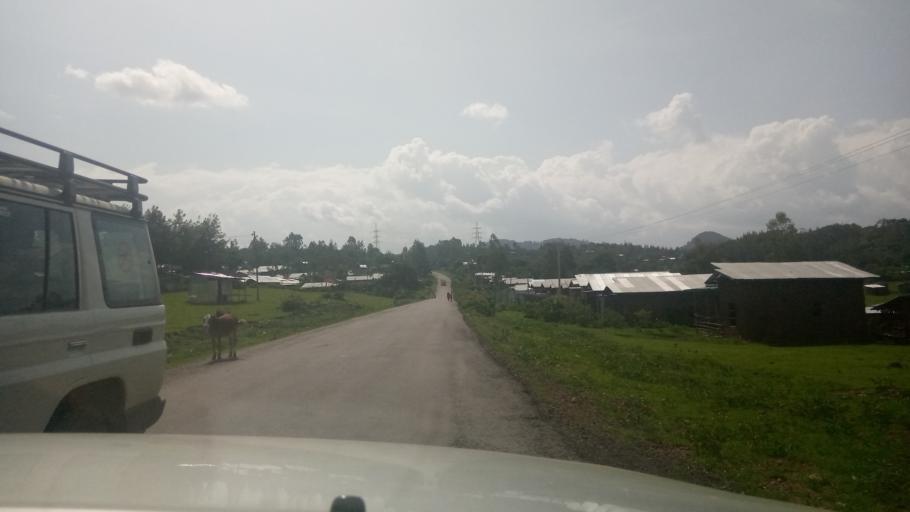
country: ET
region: Oromiya
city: Agaro
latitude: 7.9975
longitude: 36.5003
